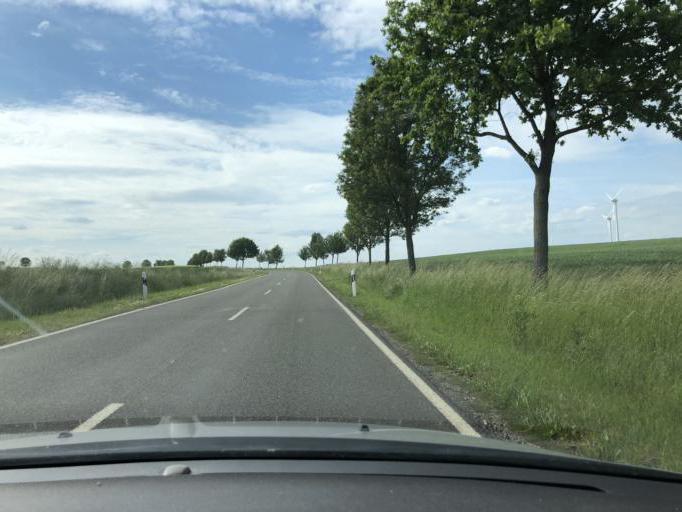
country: DE
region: Saxony
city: Nerchau
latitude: 51.2192
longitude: 12.8075
